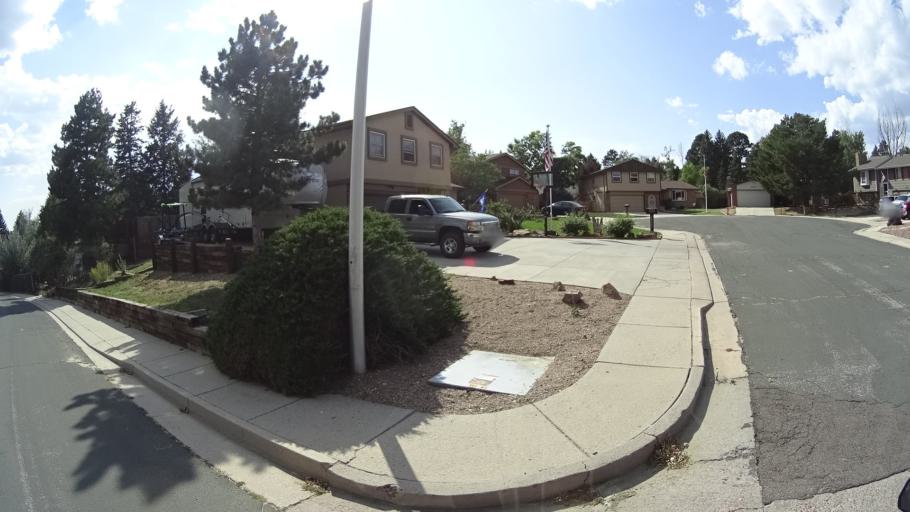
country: US
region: Colorado
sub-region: El Paso County
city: Cimarron Hills
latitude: 38.8721
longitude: -104.7251
